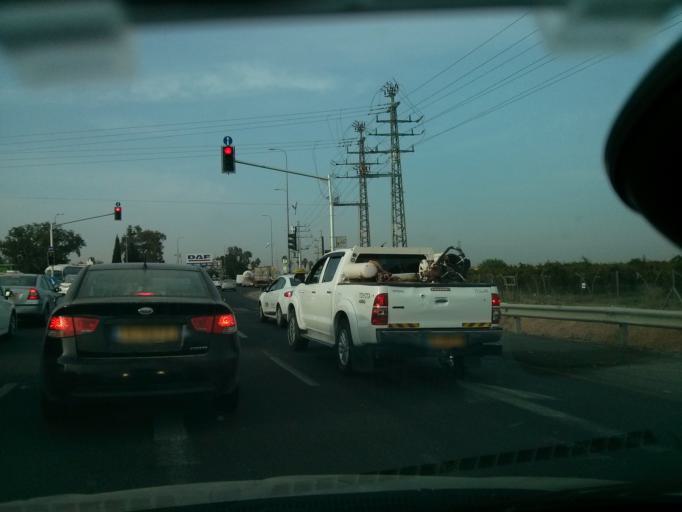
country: IL
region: Central District
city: Bene 'Ayish
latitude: 31.7607
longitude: 34.7843
